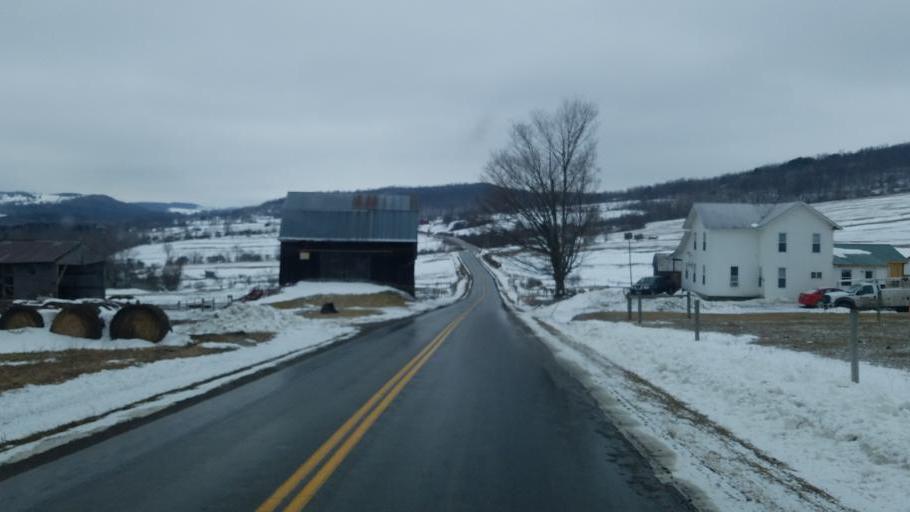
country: US
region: Pennsylvania
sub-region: Tioga County
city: Elkland
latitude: 42.0813
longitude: -77.4358
